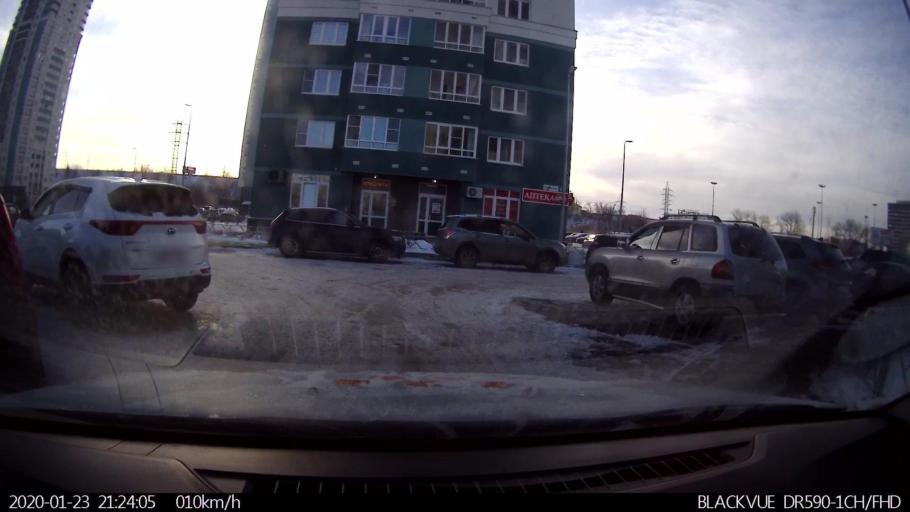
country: RU
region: Nizjnij Novgorod
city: Nizhniy Novgorod
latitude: 56.3006
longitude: 43.9515
